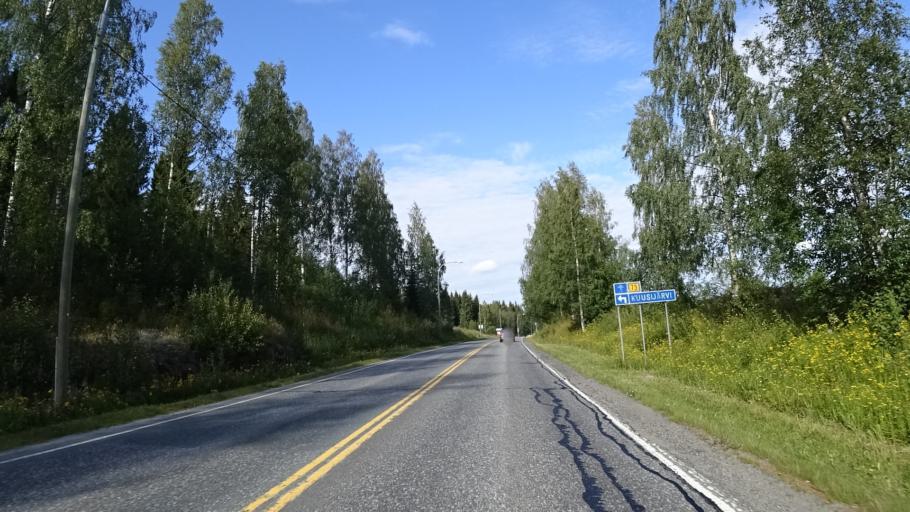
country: FI
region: North Karelia
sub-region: Joensuu
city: Eno
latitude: 62.7887
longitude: 30.0815
